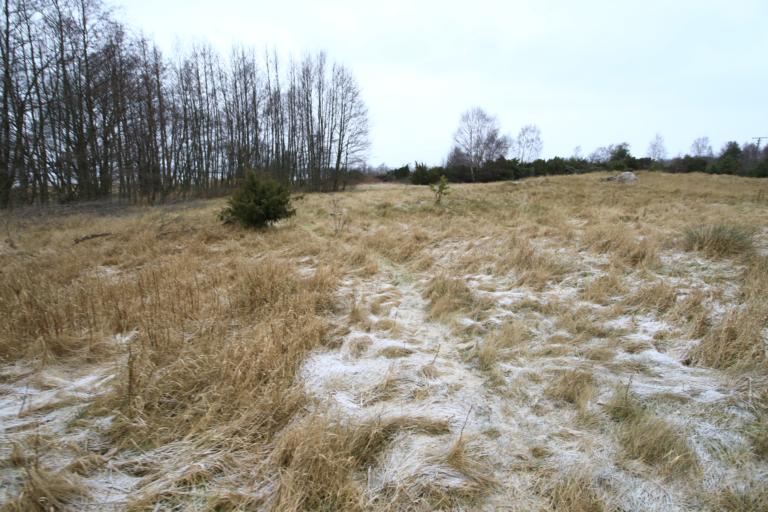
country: SE
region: Halland
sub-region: Varbergs Kommun
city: Varberg
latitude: 57.2083
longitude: 12.2107
